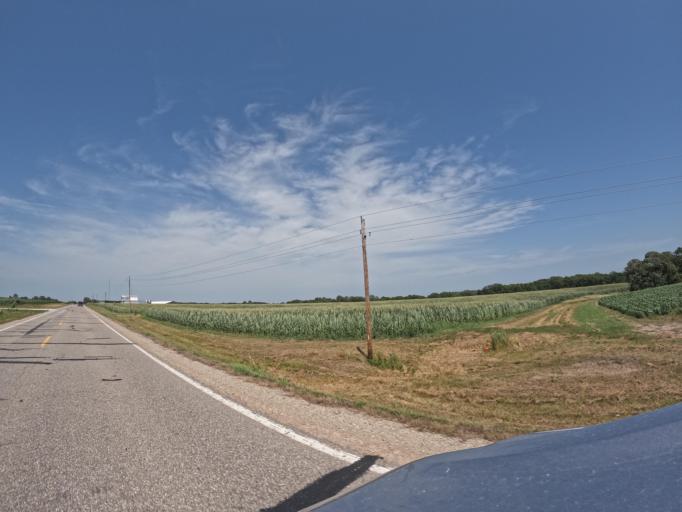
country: US
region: Iowa
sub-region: Henry County
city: Mount Pleasant
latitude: 40.9956
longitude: -91.6122
